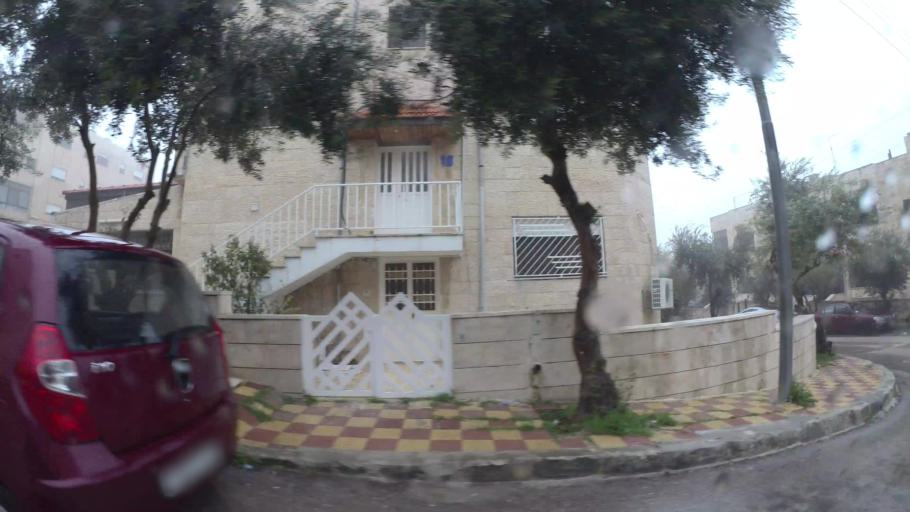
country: JO
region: Amman
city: Al Jubayhah
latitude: 32.0194
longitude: 35.8798
